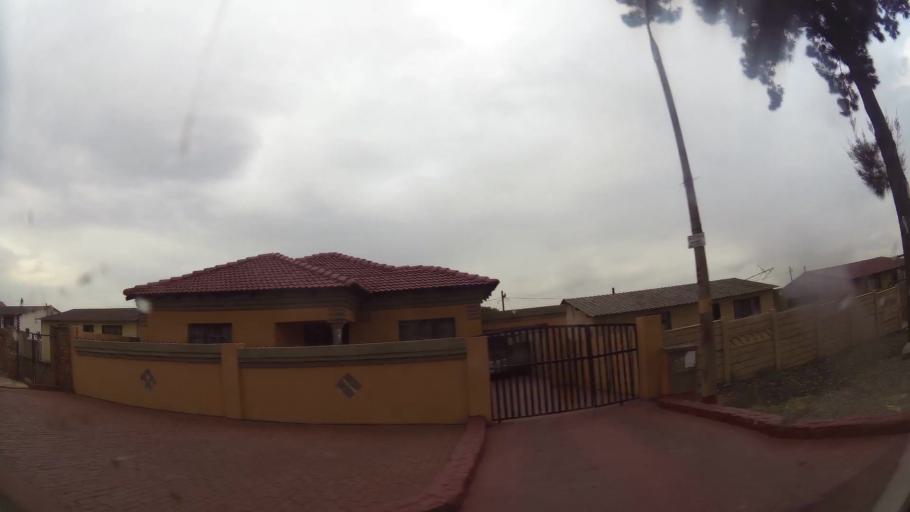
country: ZA
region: Gauteng
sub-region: Ekurhuleni Metropolitan Municipality
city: Germiston
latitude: -26.3780
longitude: 28.1304
